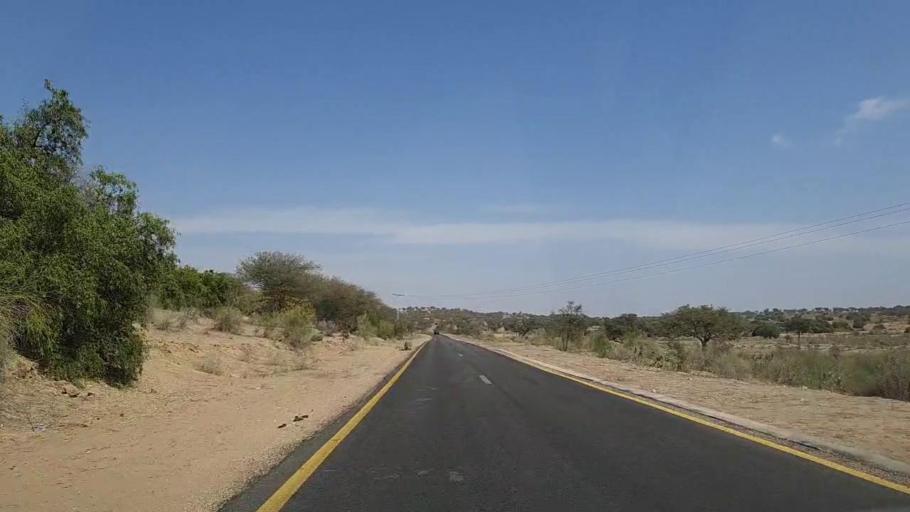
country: PK
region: Sindh
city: Mithi
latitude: 24.9014
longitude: 69.8851
